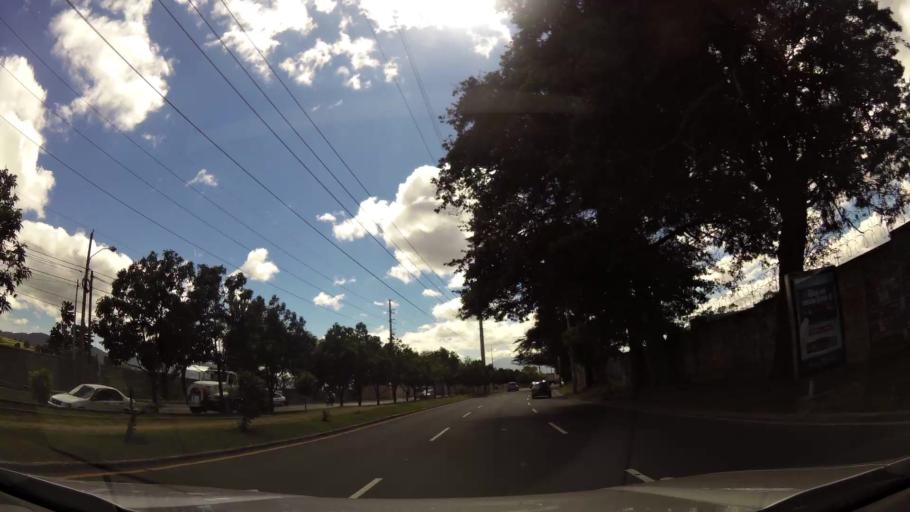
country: GT
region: Guatemala
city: Santa Catarina Pinula
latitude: 14.5723
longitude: -90.5423
